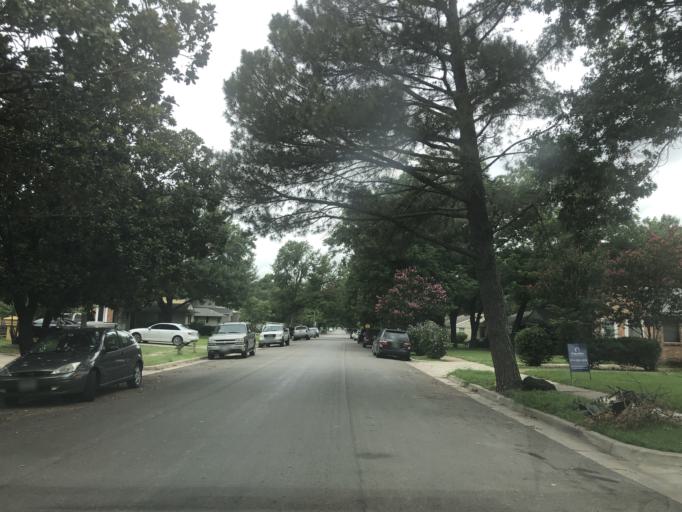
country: US
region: Texas
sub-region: Dallas County
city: University Park
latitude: 32.8707
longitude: -96.8492
